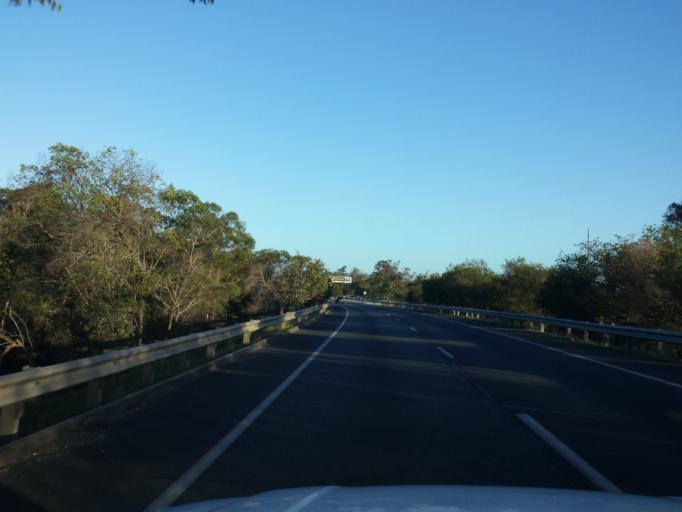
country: AU
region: Queensland
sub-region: Logan
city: Logan City
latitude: -27.6661
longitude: 153.1041
